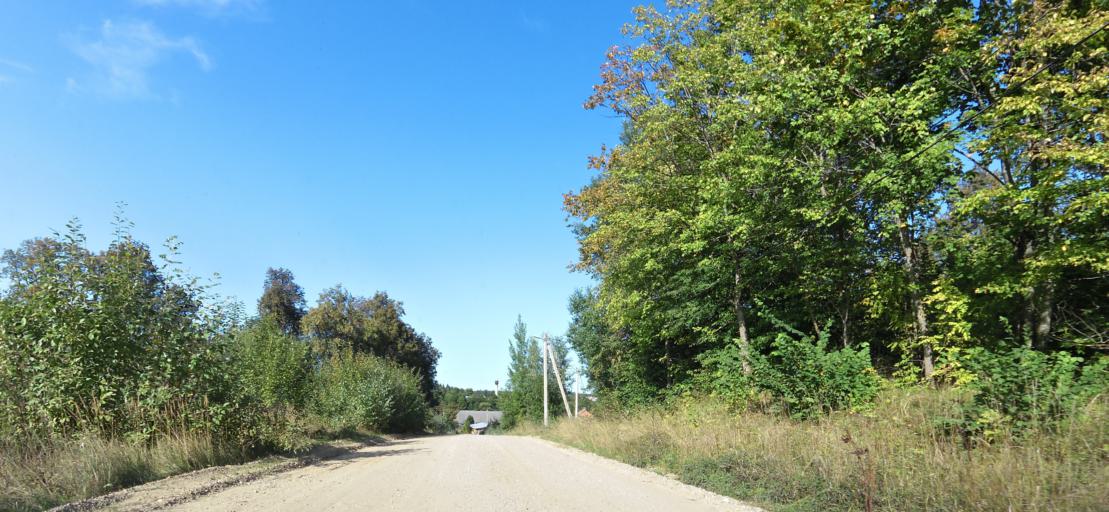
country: LT
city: Salcininkai
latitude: 54.4309
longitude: 25.3004
